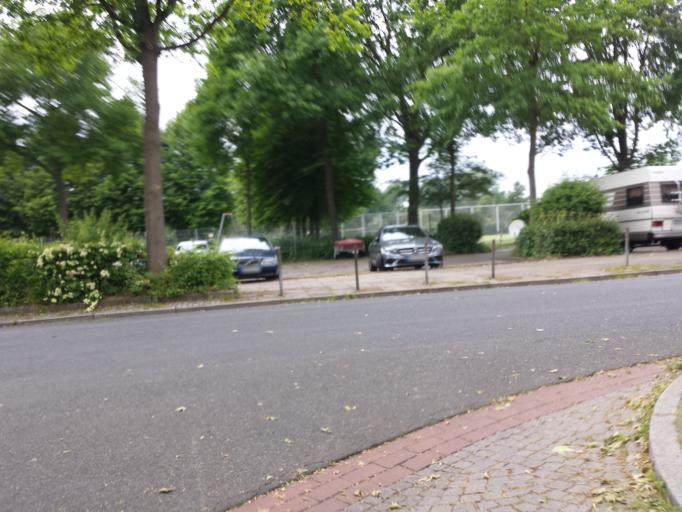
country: DE
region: Bremen
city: Bremen
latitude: 53.0980
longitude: 8.7993
